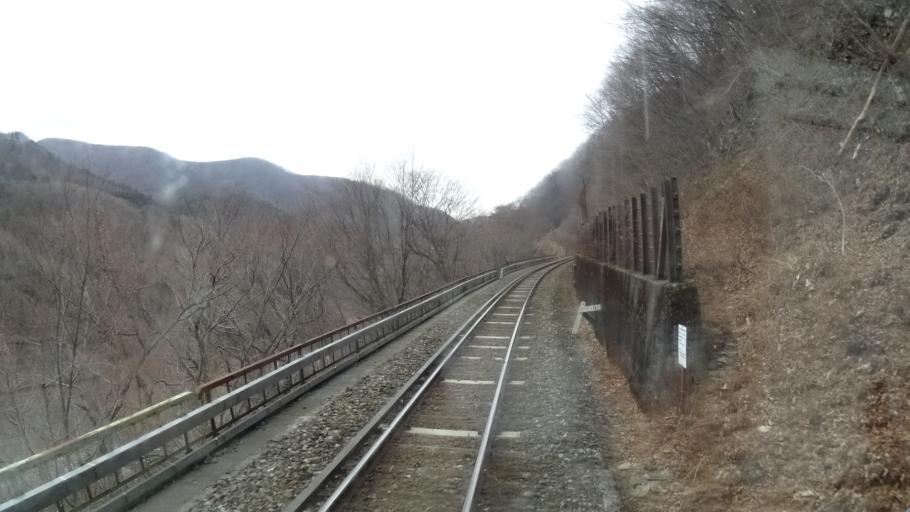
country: JP
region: Iwate
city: Kamaishi
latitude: 39.2773
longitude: 141.7187
